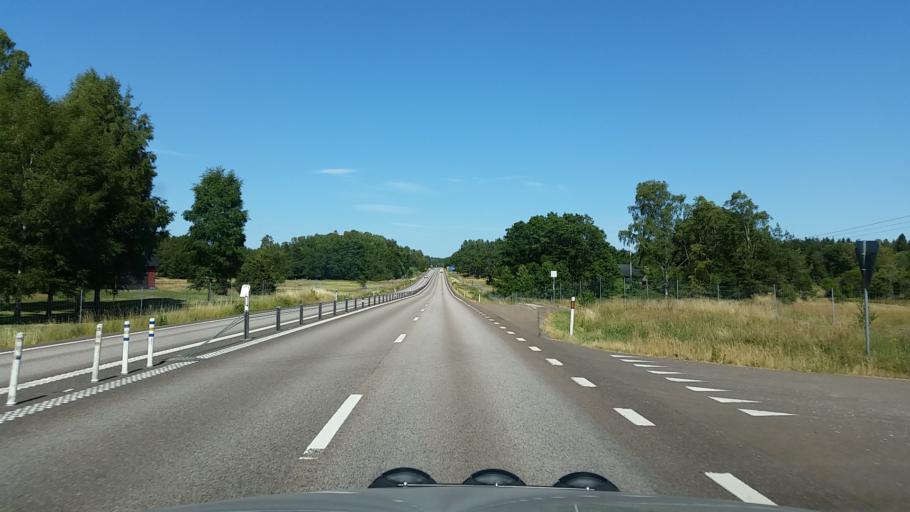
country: SE
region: Vaestra Goetaland
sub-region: Melleruds Kommun
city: Mellerud
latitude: 58.8353
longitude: 12.5379
